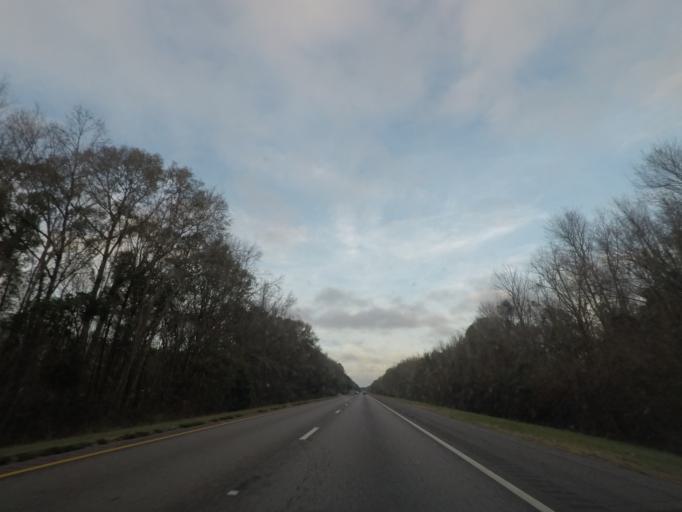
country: US
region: South Carolina
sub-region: Orangeburg County
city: Holly Hill
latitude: 33.3401
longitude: -80.5351
